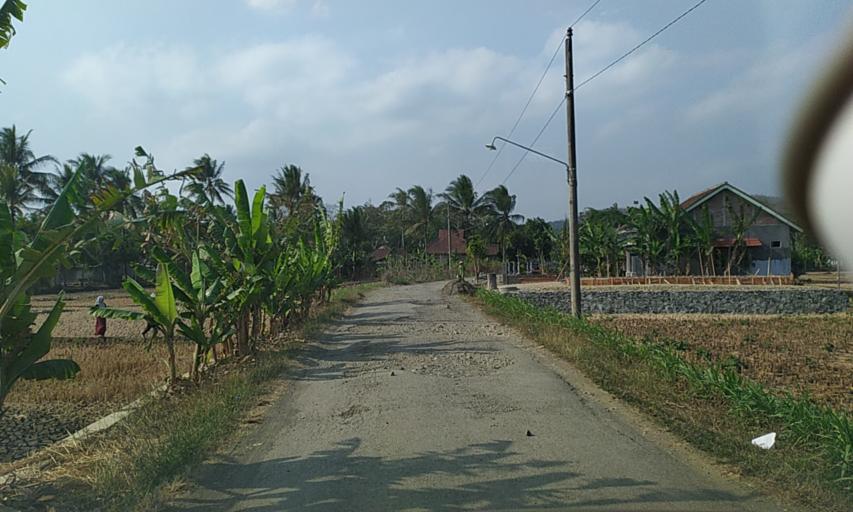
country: ID
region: Central Java
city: Karanggintung
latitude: -7.4826
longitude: 108.9125
